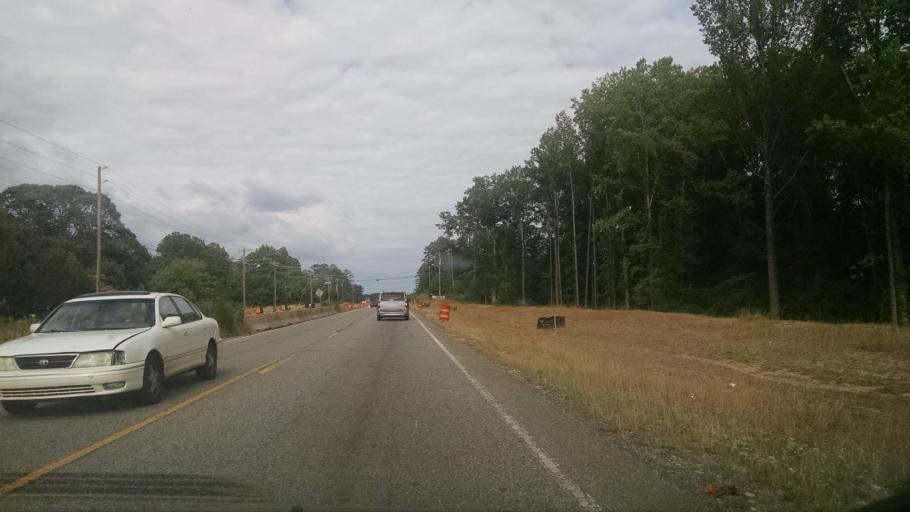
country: US
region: Georgia
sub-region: Gwinnett County
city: Sugar Hill
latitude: 34.1121
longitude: -84.0686
